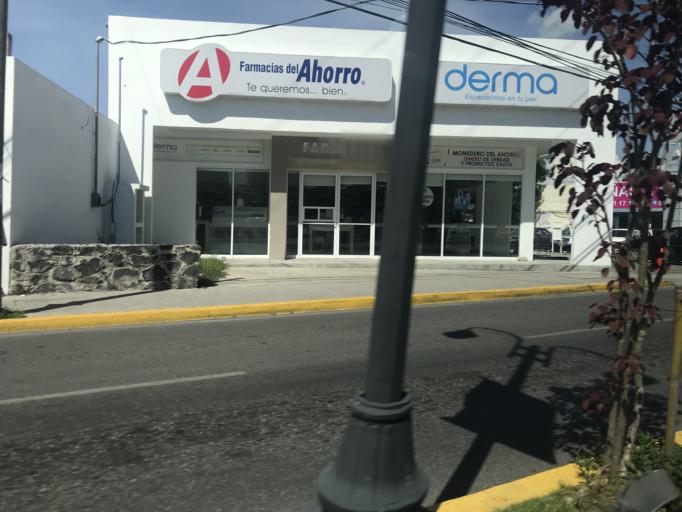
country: MX
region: Puebla
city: San Andres Cholula
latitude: 19.0576
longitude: -98.2963
